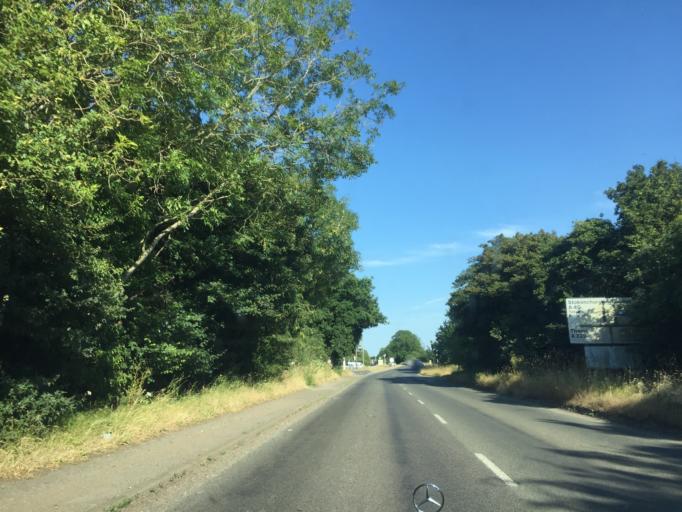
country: GB
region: England
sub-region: Oxfordshire
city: Chalgrove
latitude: 51.7260
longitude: -1.0581
